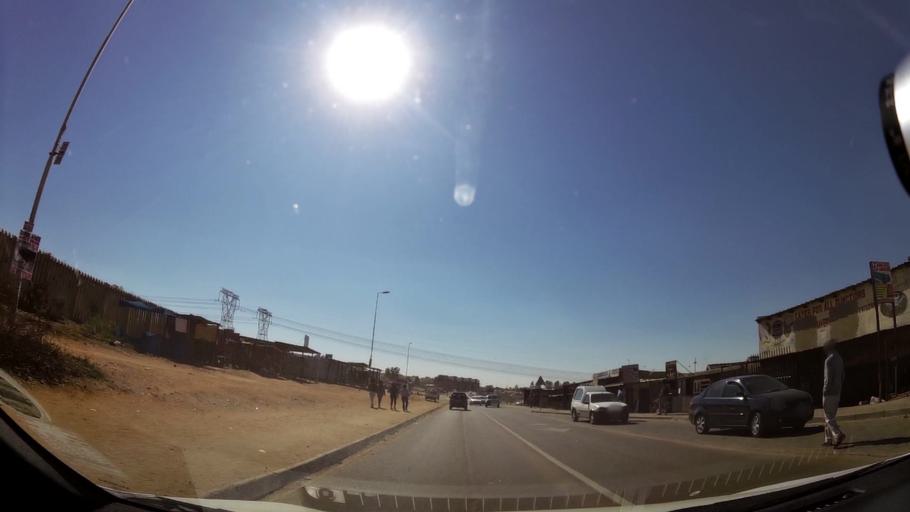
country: ZA
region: Gauteng
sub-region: City of Johannesburg Metropolitan Municipality
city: Diepsloot
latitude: -25.9062
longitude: 28.0957
